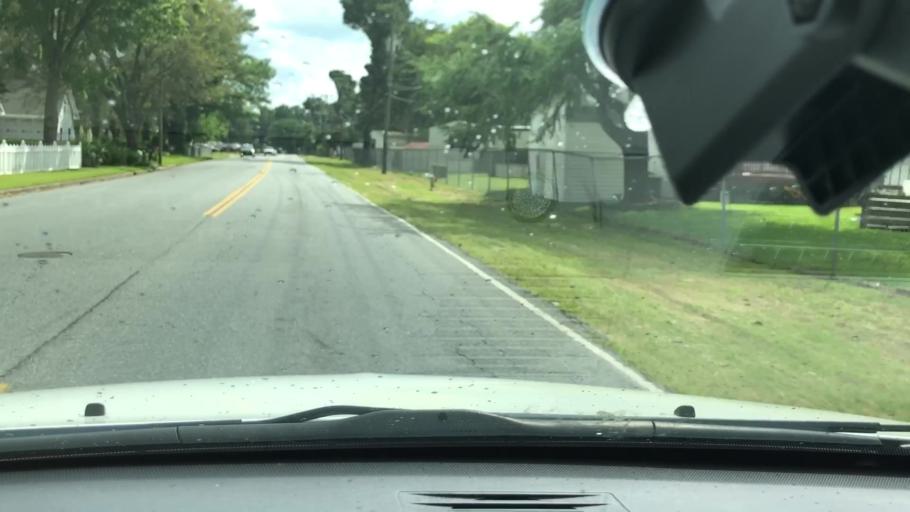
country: US
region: Virginia
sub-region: City of Chesapeake
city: Chesapeake
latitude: 36.7835
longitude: -76.2674
